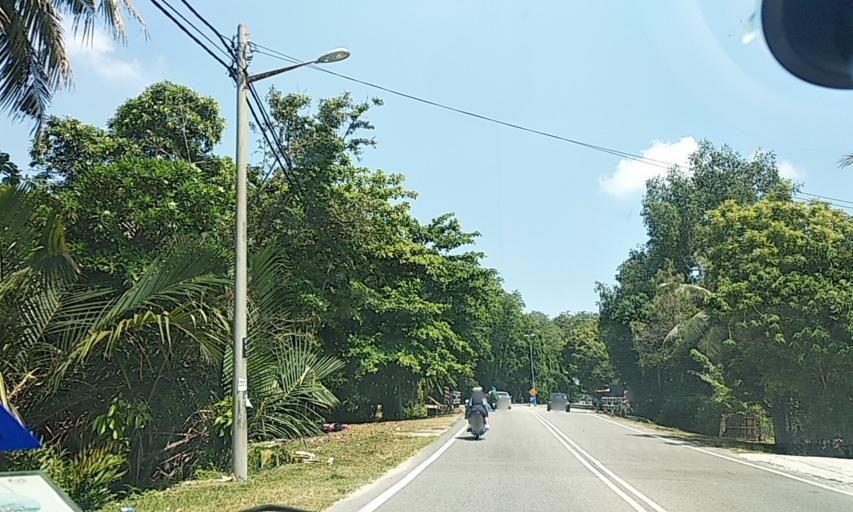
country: MY
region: Kedah
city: Sungai Petani
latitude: 5.6347
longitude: 100.4796
